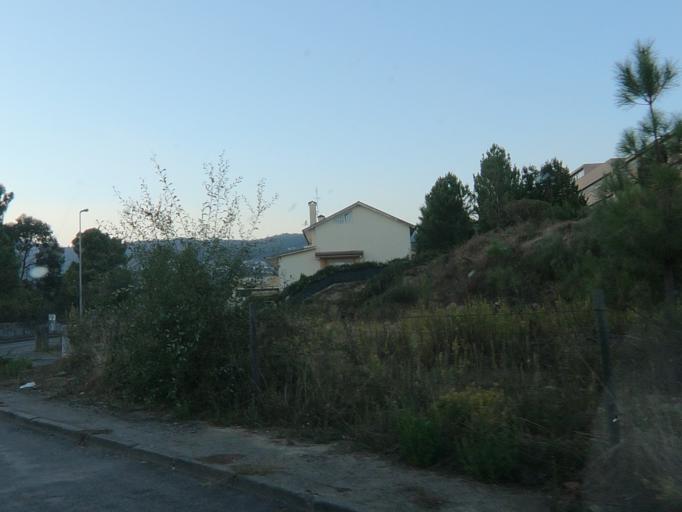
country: PT
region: Vila Real
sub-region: Vila Real
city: Vila Real
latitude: 41.3054
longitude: -7.7666
